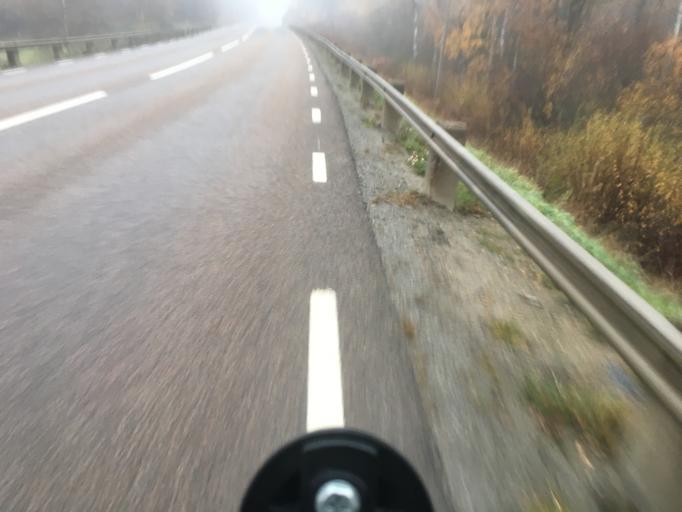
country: SE
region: Blekinge
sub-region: Karlshamns Kommun
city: Morrum
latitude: 56.1861
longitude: 14.7664
